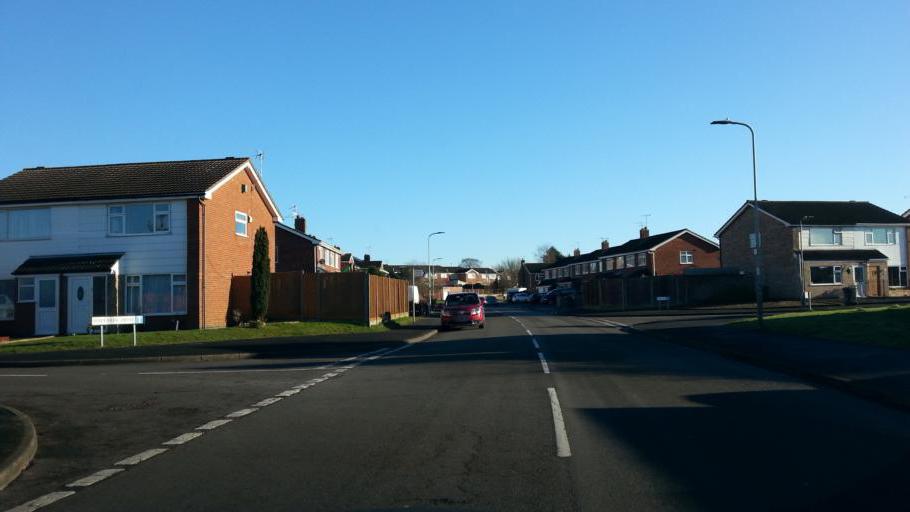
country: GB
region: England
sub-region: Leicestershire
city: Queniborough
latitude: 52.7162
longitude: -1.0516
